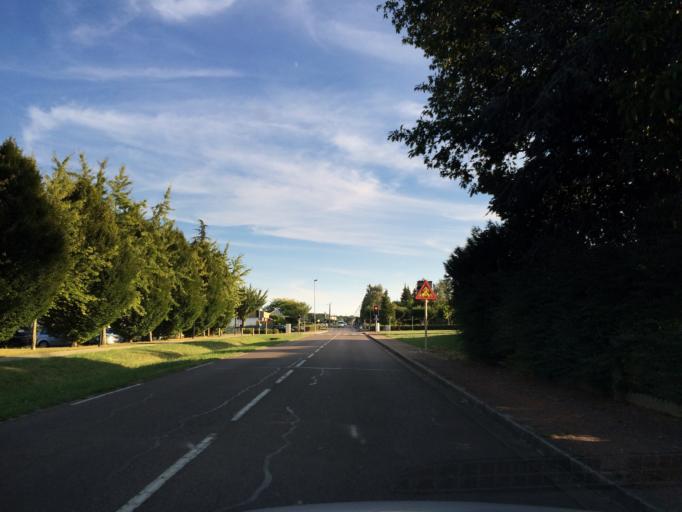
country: FR
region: Bourgogne
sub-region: Departement de l'Yonne
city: Saint-Georges-sur-Baulche
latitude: 47.8226
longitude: 3.5394
